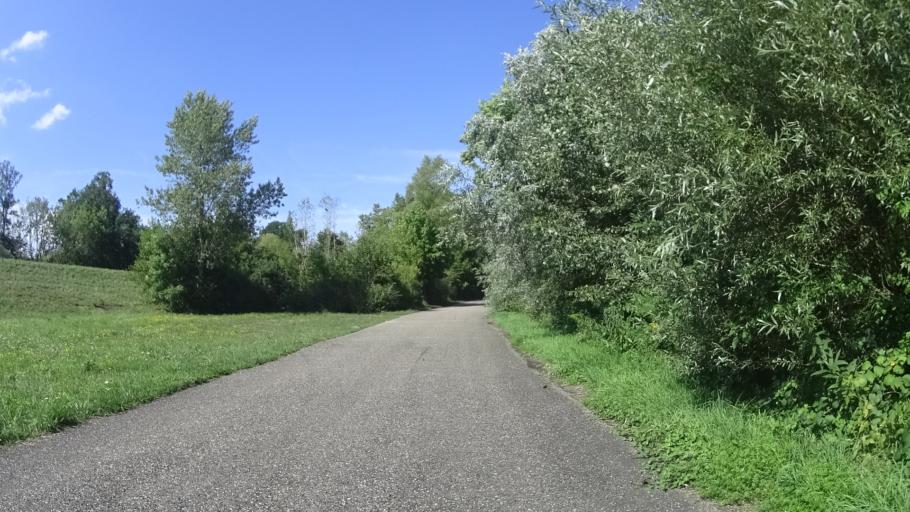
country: DE
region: Baden-Wuerttemberg
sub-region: Karlsruhe Region
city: Hugelsheim
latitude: 48.8372
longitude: 8.1030
